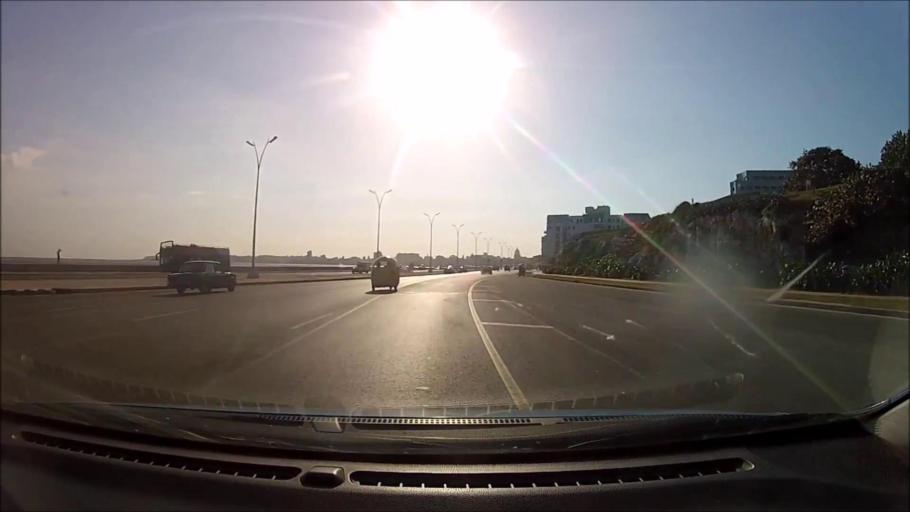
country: CU
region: La Habana
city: Havana
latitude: 23.1445
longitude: -82.3793
